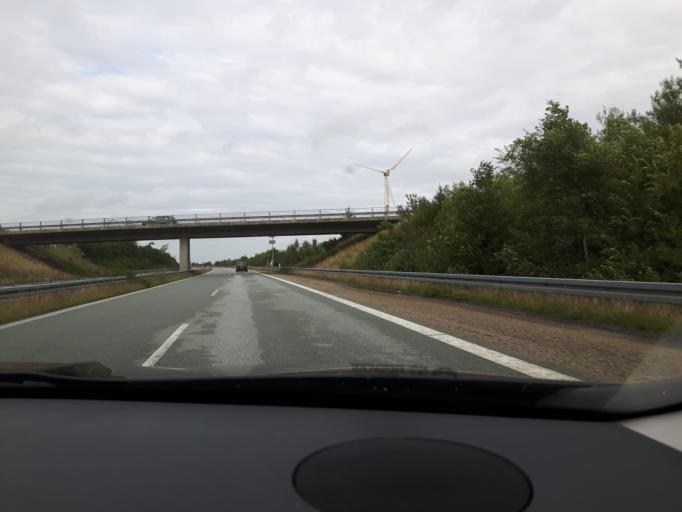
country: DK
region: North Denmark
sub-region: Hjorring Kommune
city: Hjorring
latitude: 57.4818
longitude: 10.0372
